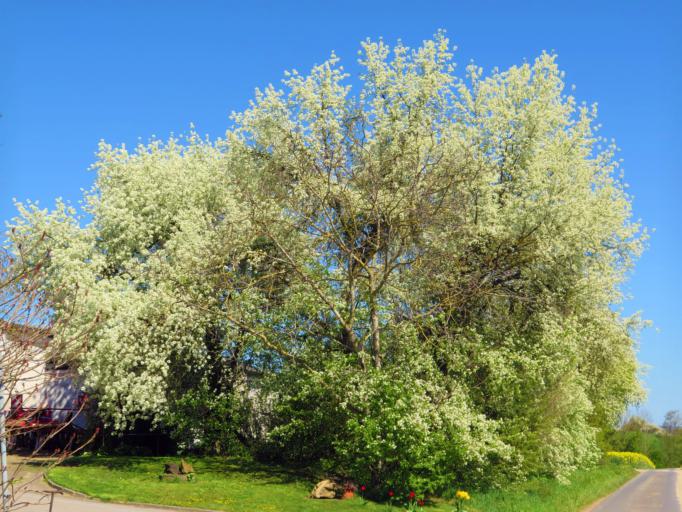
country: DE
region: Bavaria
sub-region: Regierungsbezirk Unterfranken
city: Wonfurt
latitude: 50.0194
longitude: 10.4284
